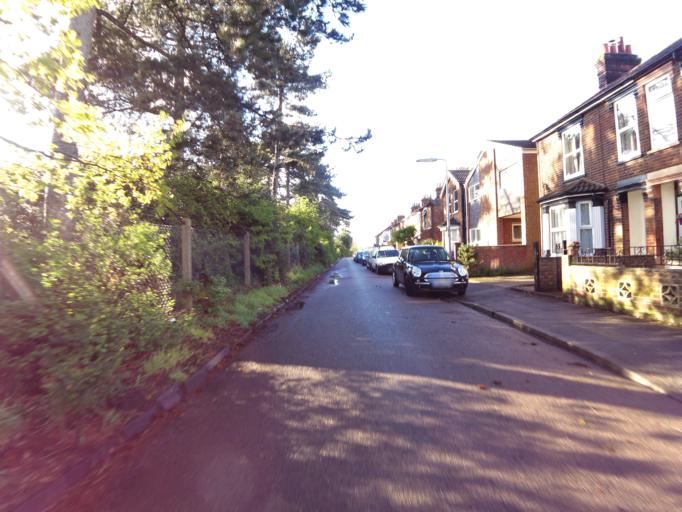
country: GB
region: England
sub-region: Suffolk
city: Ipswich
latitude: 52.0501
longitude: 1.1836
